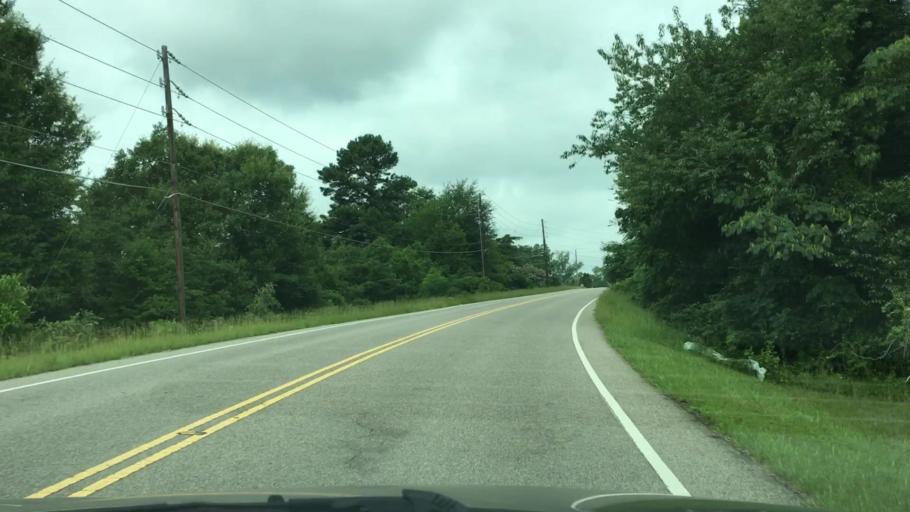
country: US
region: South Carolina
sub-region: Aiken County
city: Belvedere
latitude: 33.5510
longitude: -81.9549
